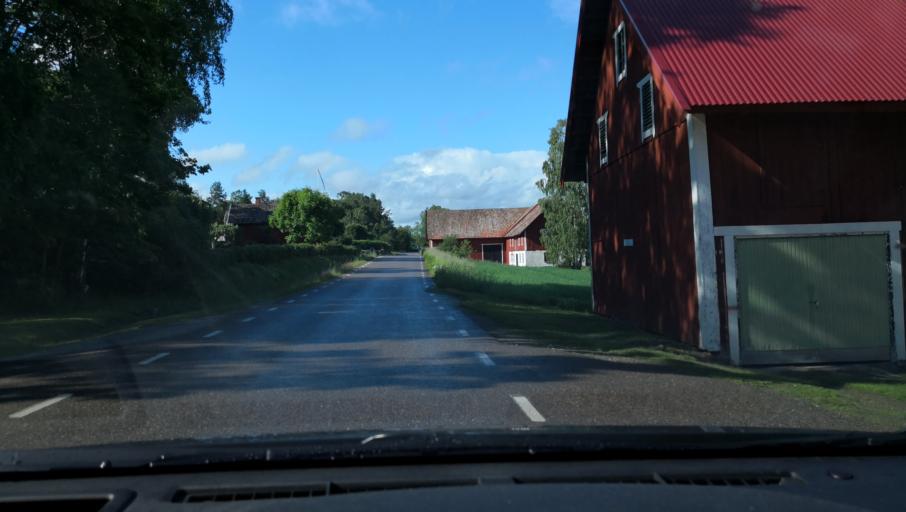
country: SE
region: OErebro
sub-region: Lindesbergs Kommun
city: Fellingsbro
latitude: 59.3138
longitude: 15.6784
